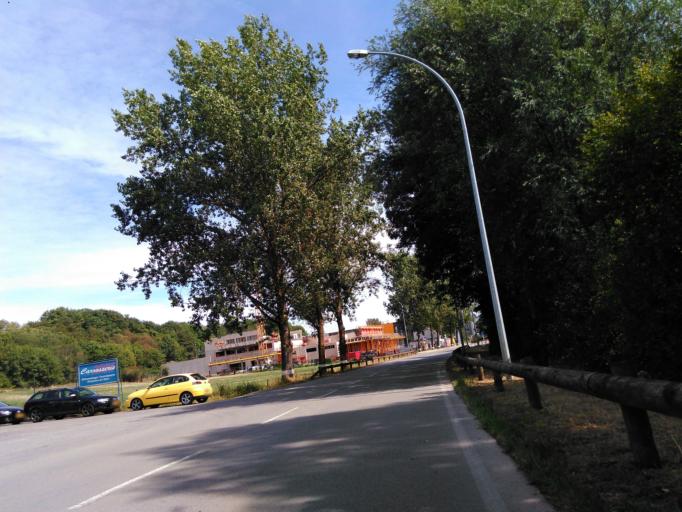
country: LU
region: Luxembourg
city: Fentange
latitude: 49.5599
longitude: 6.1470
